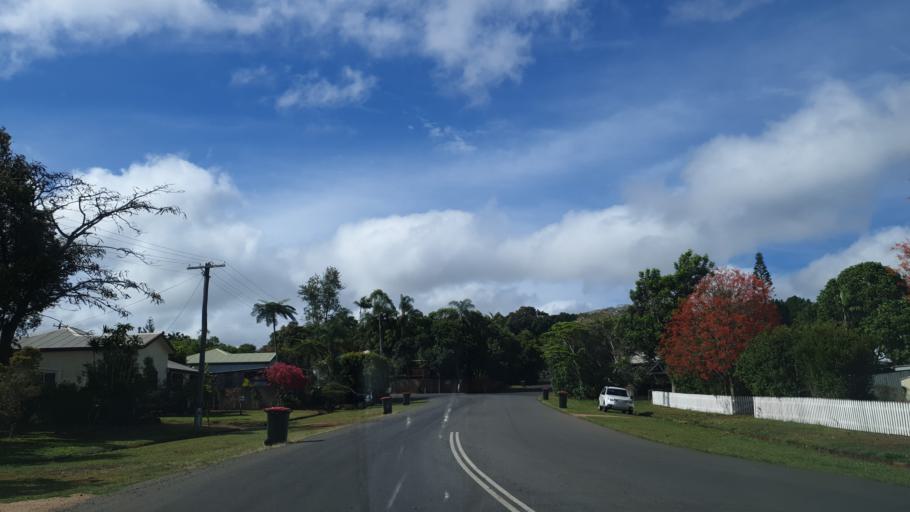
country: AU
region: Queensland
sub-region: Tablelands
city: Atherton
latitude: -17.3519
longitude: 145.5913
